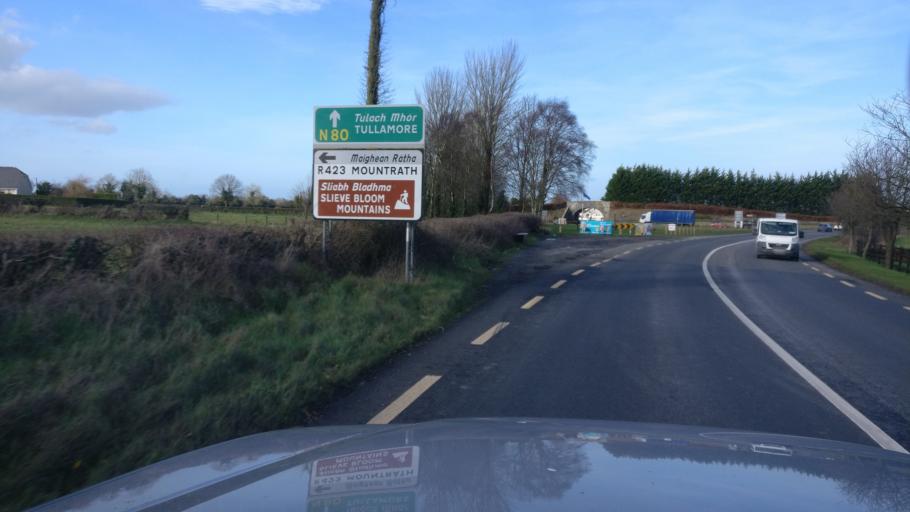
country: IE
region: Leinster
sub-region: Laois
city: Mountmellick
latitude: 53.1001
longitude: -7.3388
